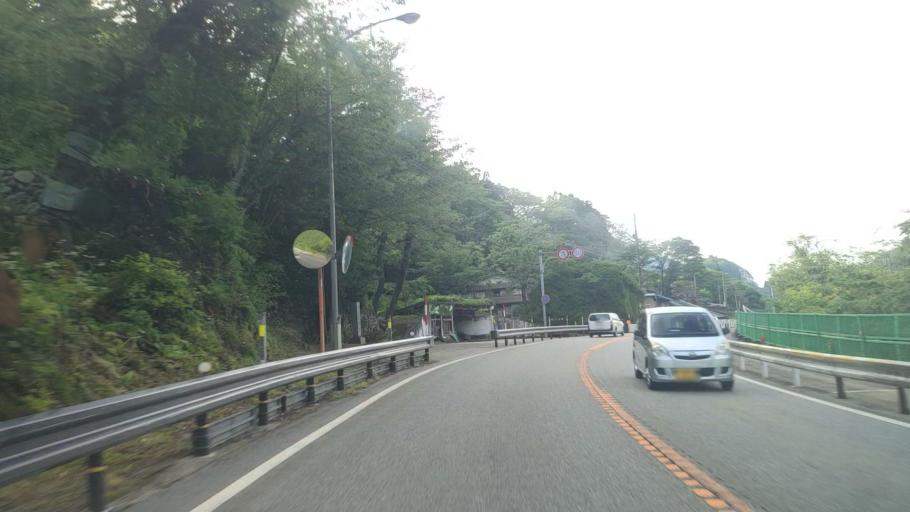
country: JP
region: Toyama
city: Yatsuomachi-higashikumisaka
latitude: 36.4553
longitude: 137.2521
